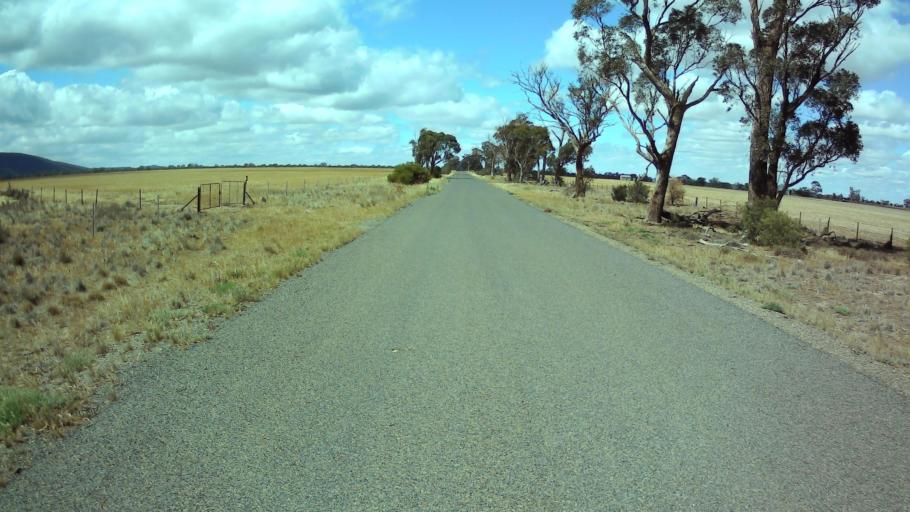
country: AU
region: New South Wales
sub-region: Weddin
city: Grenfell
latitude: -33.8757
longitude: 147.9252
